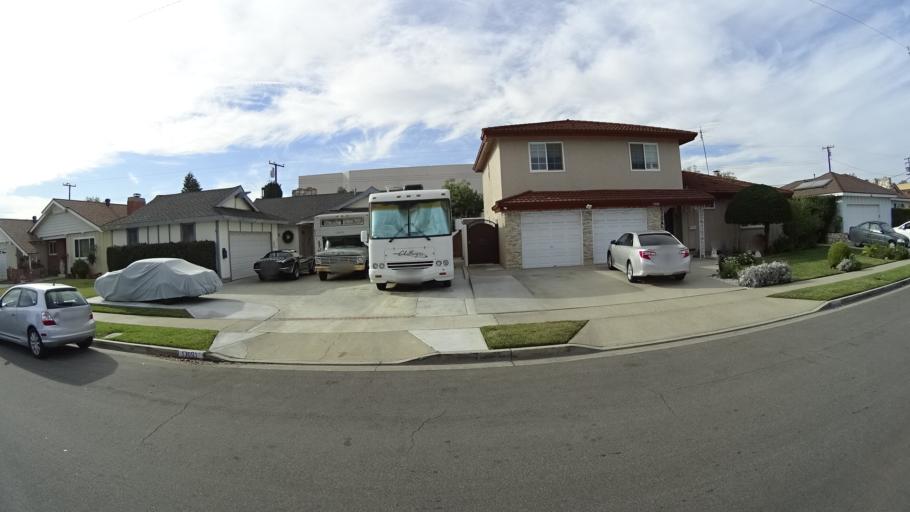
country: US
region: California
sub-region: Orange County
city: Garden Grove
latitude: 33.7729
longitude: -117.9178
